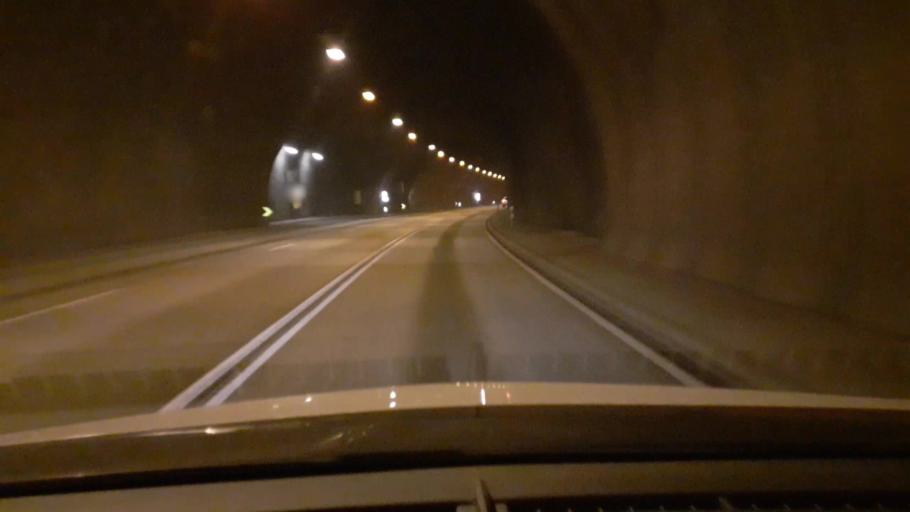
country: IS
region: Capital Region
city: Reykjavik
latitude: 64.3056
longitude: -21.8940
